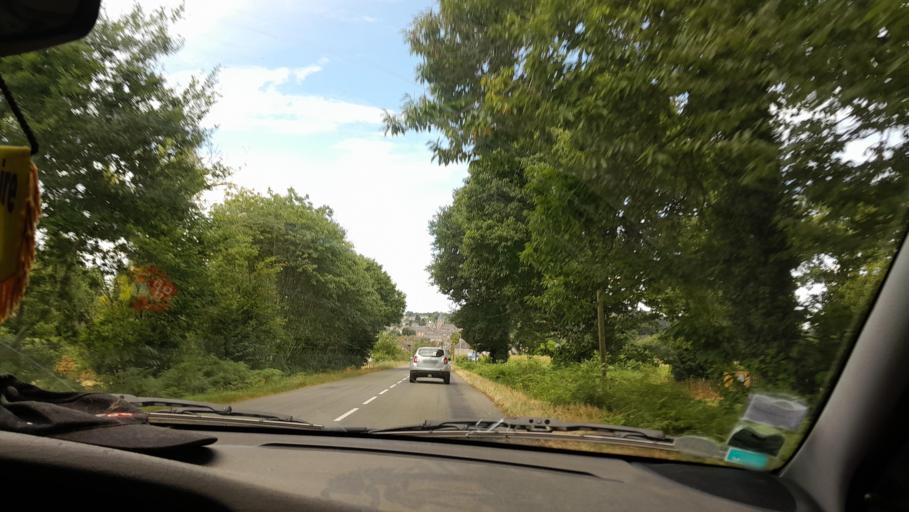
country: FR
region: Brittany
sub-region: Departement d'Ille-et-Vilaine
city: Luitre
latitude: 48.2619
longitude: -1.1344
